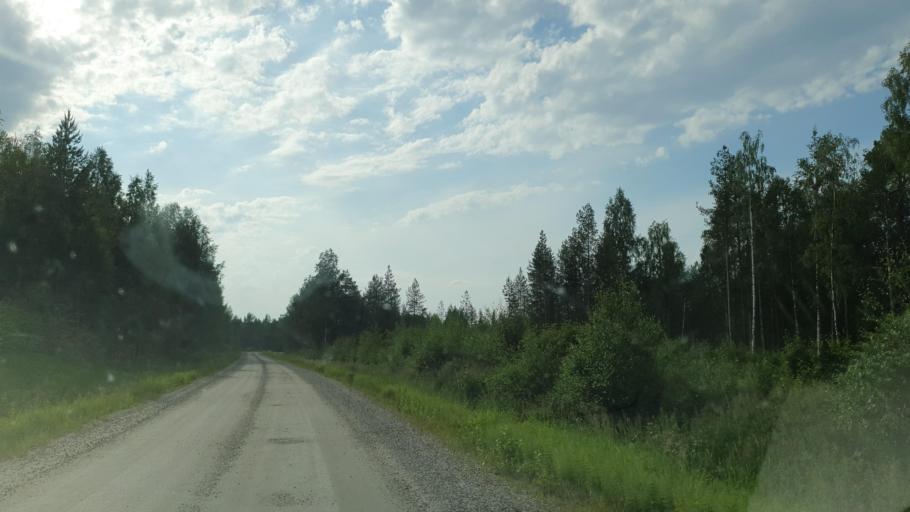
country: FI
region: Kainuu
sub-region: Kehys-Kainuu
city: Kuhmo
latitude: 64.0789
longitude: 29.7062
